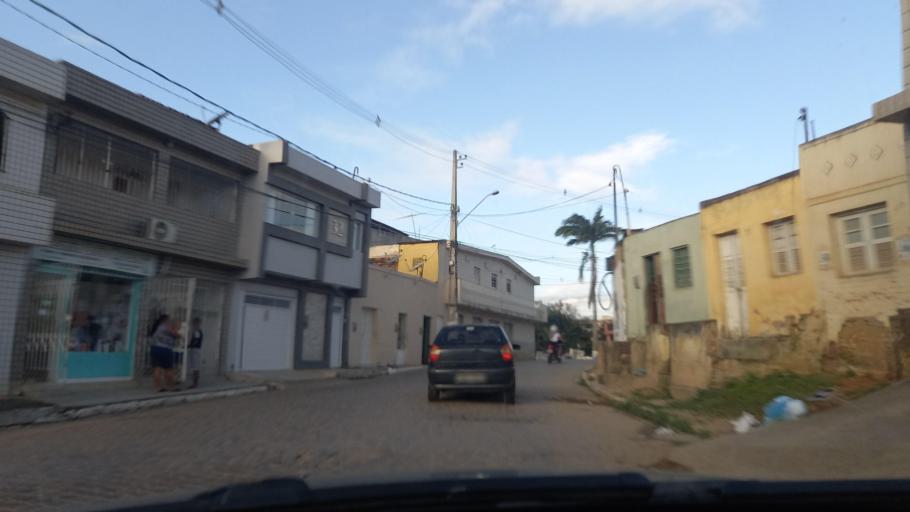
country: BR
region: Pernambuco
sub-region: Vitoria De Santo Antao
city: Vitoria de Santo Antao
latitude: -8.1238
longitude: -35.2968
